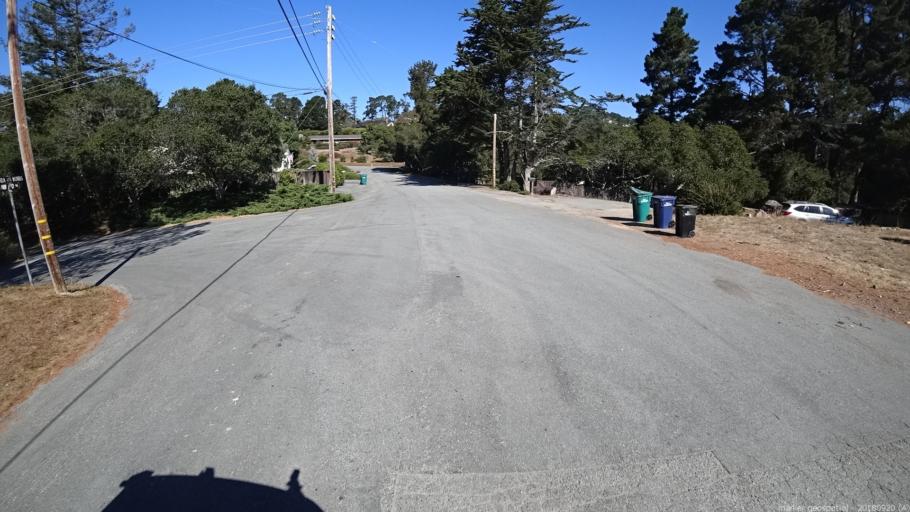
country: US
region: California
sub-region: Monterey County
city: Carmel-by-the-Sea
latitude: 36.5541
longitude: -121.8991
